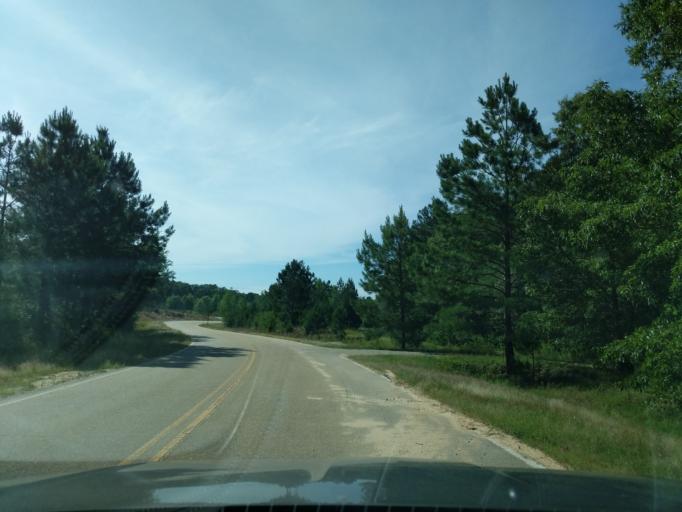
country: US
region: Georgia
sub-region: Jefferson County
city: Wrens
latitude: 33.2300
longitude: -82.3535
